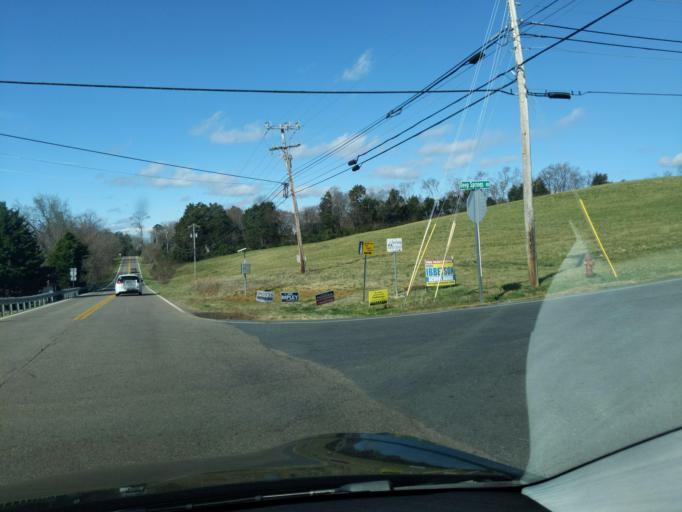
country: US
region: Tennessee
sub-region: Jefferson County
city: Dandridge
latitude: 35.9715
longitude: -83.5045
